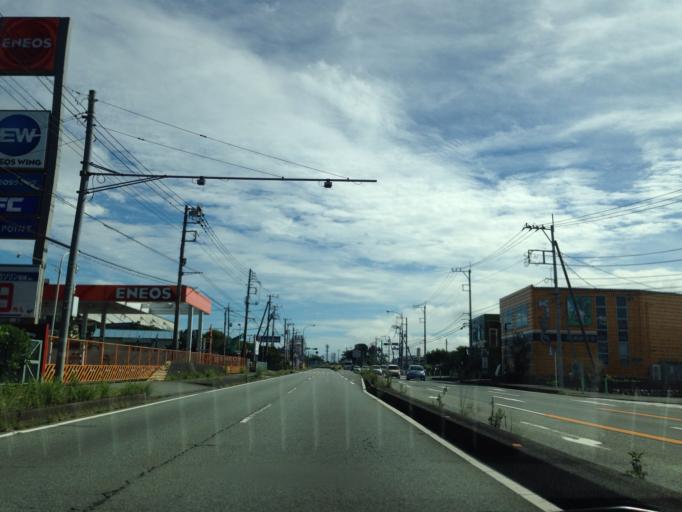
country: JP
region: Shizuoka
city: Gotemba
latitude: 35.2757
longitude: 138.9144
